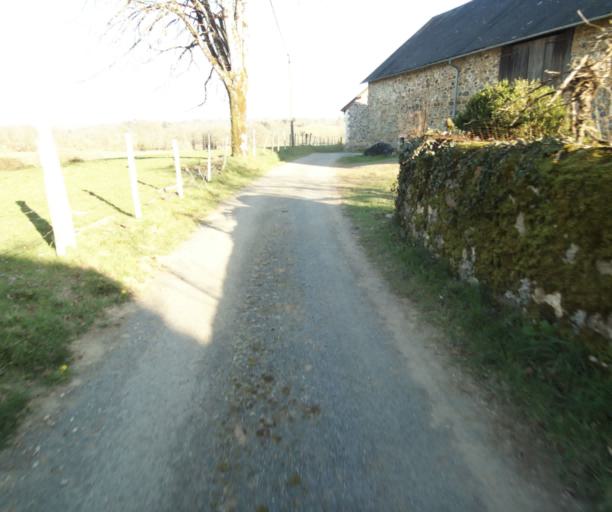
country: FR
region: Limousin
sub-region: Departement de la Correze
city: Saint-Clement
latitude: 45.3359
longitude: 1.6567
